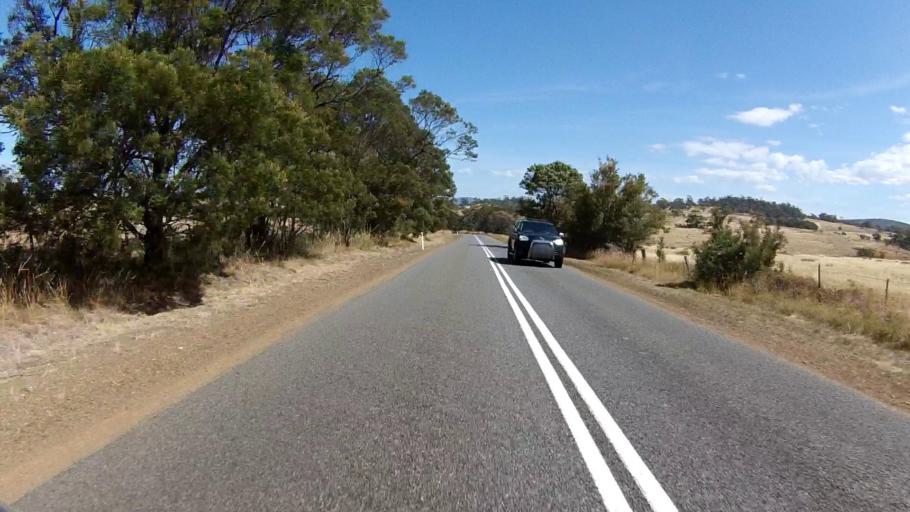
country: AU
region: Tasmania
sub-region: Sorell
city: Sorell
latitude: -42.2907
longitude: 147.9920
